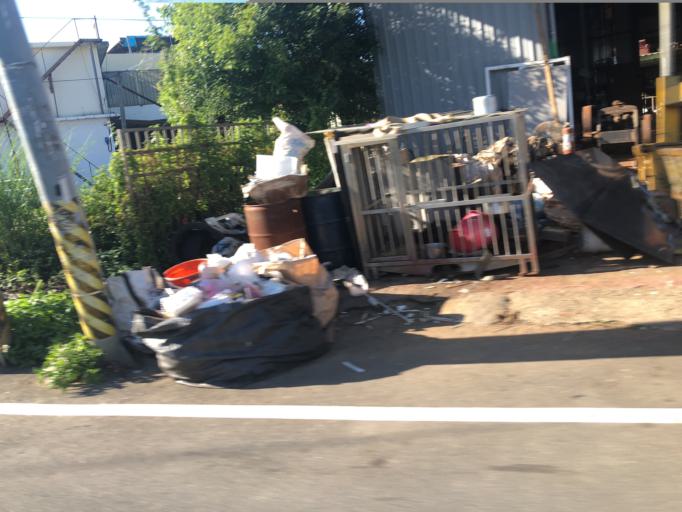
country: TW
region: Taiwan
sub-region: Hsinchu
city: Hsinchu
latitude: 24.7302
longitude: 120.9375
